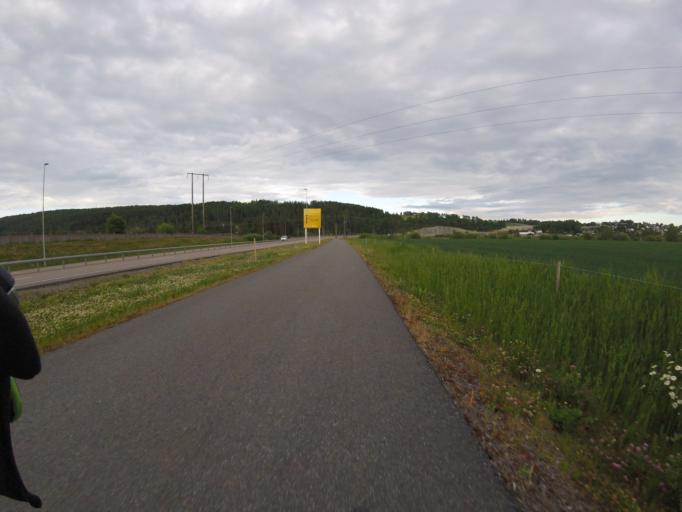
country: NO
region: Akershus
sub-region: Fet
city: Fetsund
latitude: 59.9409
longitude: 11.1226
